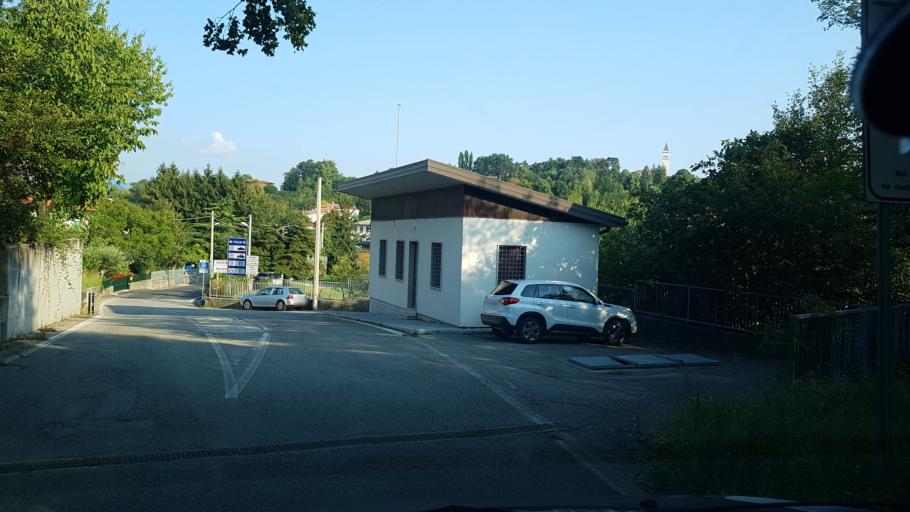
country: IT
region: Friuli Venezia Giulia
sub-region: Provincia di Gorizia
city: San Floriano del Collio
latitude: 45.9859
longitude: 13.5833
